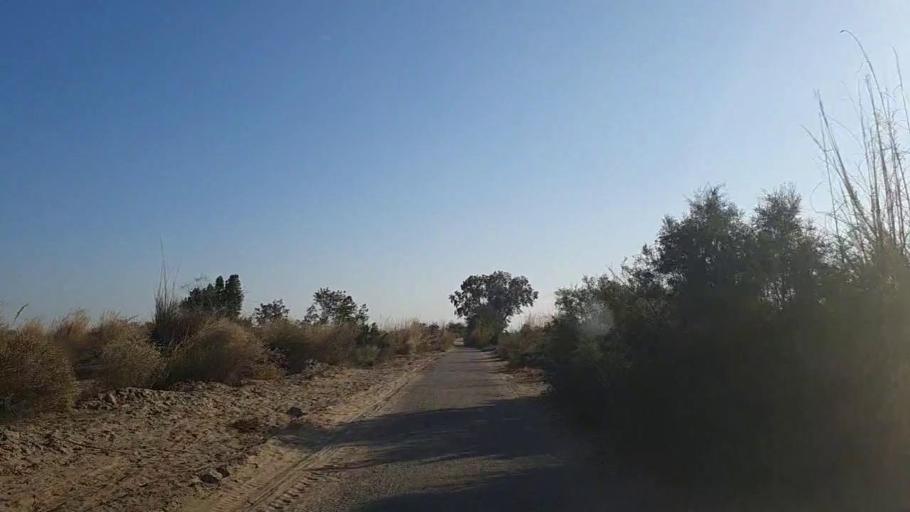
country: PK
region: Sindh
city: Khadro
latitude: 26.2742
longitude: 68.8604
